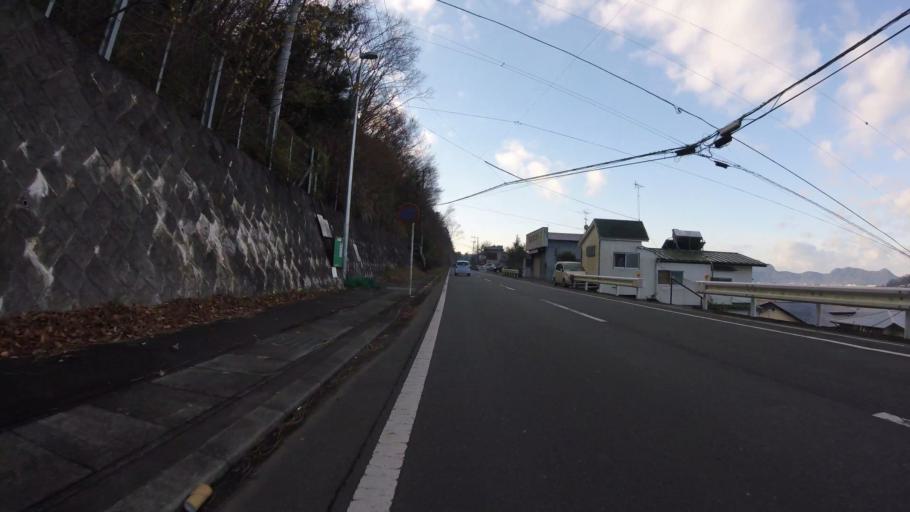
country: JP
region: Shizuoka
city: Mishima
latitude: 35.1013
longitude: 138.9641
